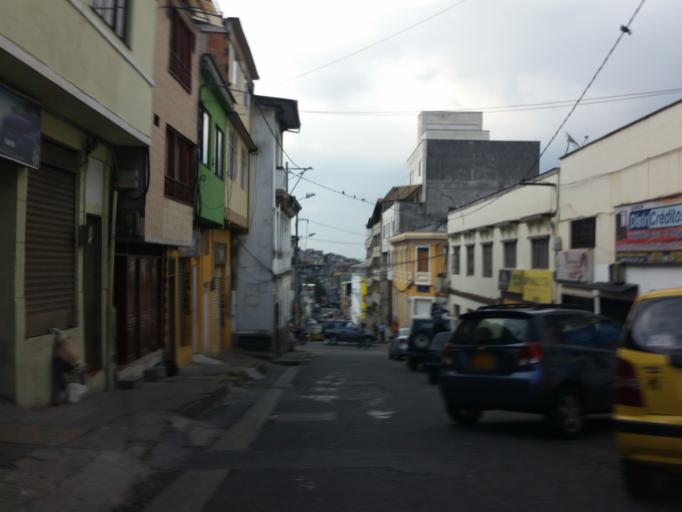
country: CO
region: Caldas
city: Manizales
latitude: 5.0654
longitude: -75.5148
